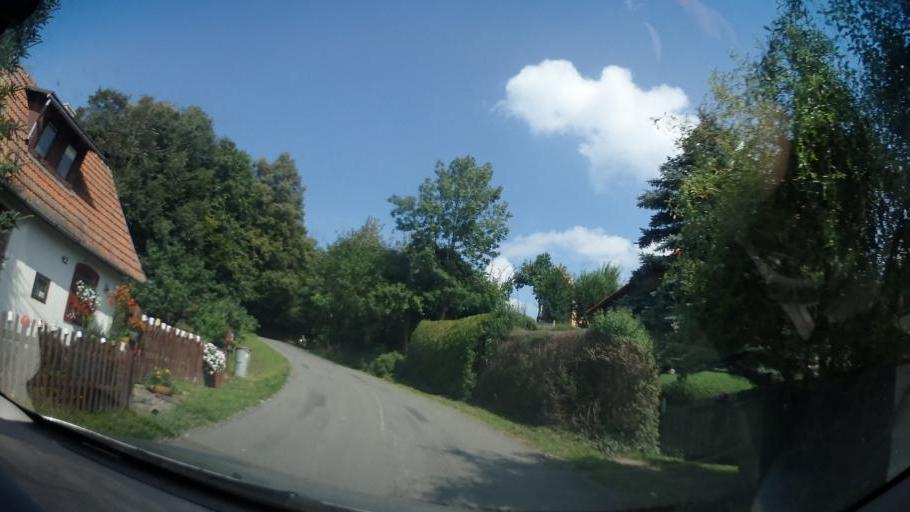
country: CZ
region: South Moravian
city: Olesnice
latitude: 49.5443
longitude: 16.3626
